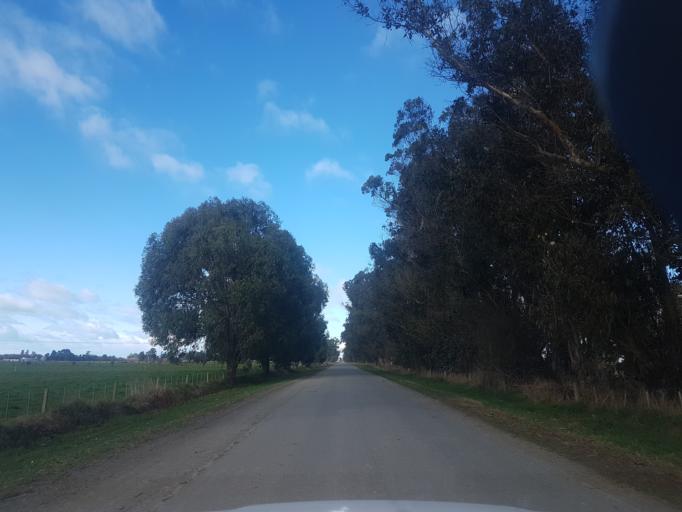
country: NZ
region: Canterbury
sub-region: Timaru District
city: Pleasant Point
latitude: -44.2088
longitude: 171.2096
